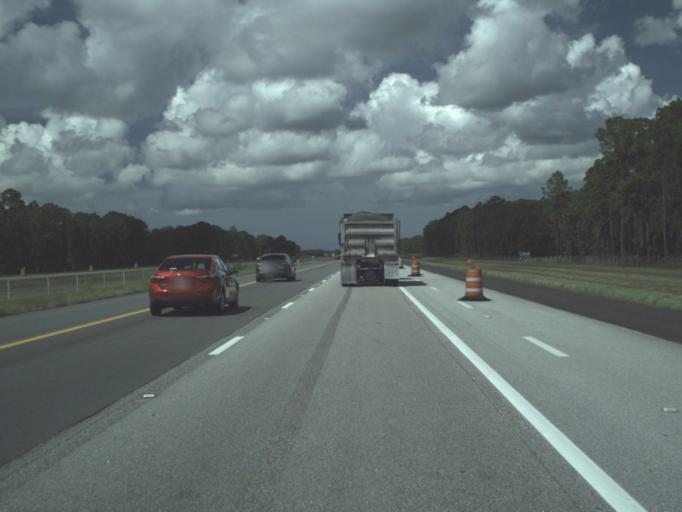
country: US
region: Florida
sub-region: Sarasota County
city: Warm Mineral Springs
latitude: 27.1001
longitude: -82.2562
